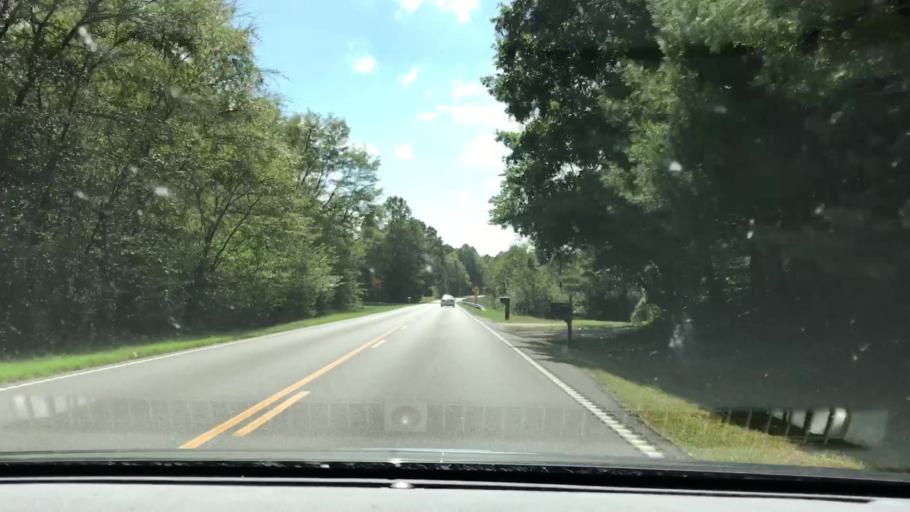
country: US
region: Kentucky
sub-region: McCracken County
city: Reidland
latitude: 36.9774
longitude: -88.5155
